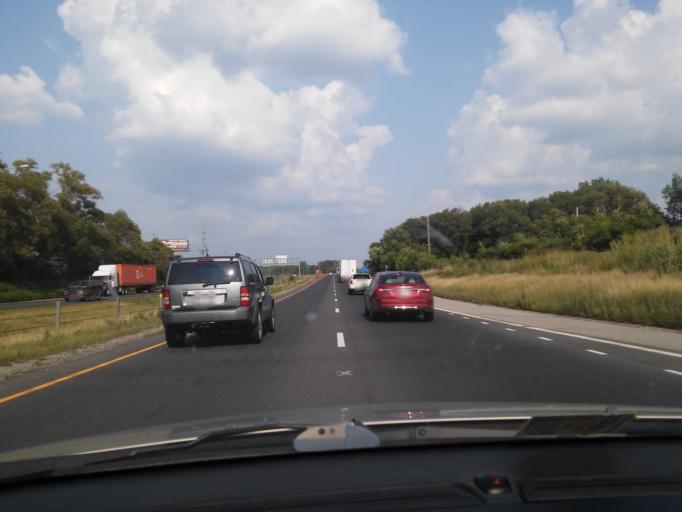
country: US
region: Illinois
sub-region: Will County
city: Joliet
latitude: 41.5131
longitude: -88.0678
